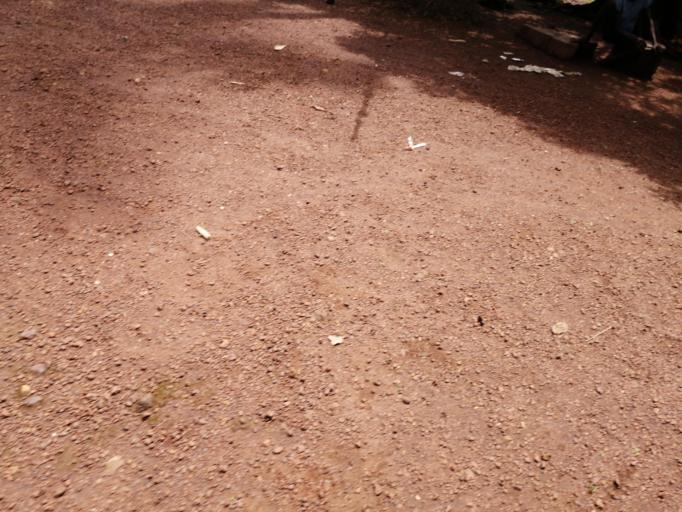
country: SL
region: Northern Province
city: Port Loko
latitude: 8.7763
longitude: -12.7979
